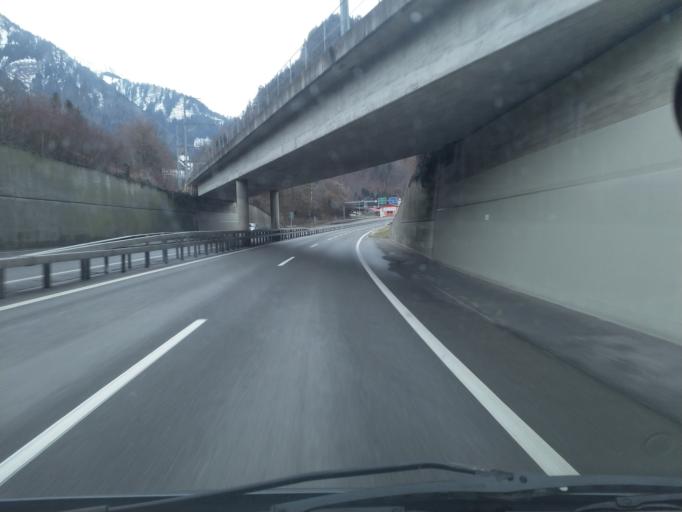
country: CH
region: Bern
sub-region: Frutigen-Niedersimmental District
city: Wimmis
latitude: 46.6779
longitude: 7.6383
